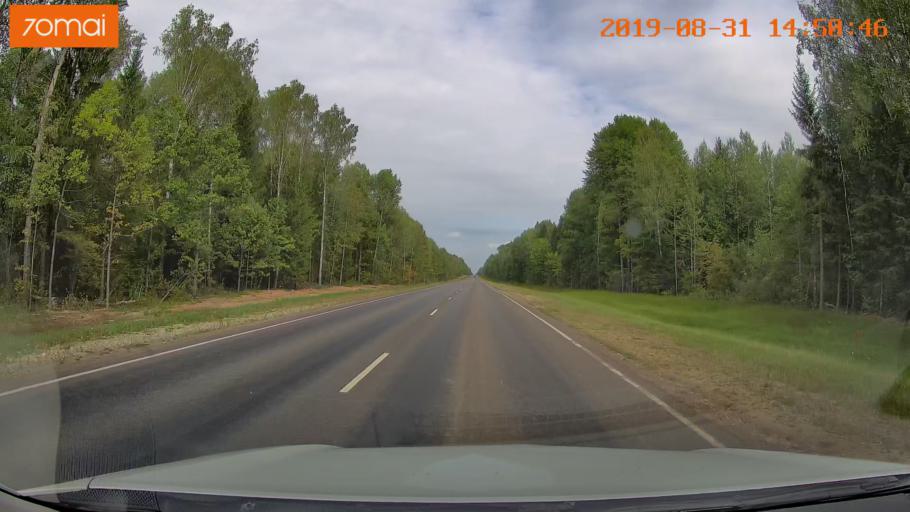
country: RU
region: Kaluga
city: Spas-Demensk
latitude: 54.2638
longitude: 33.7979
